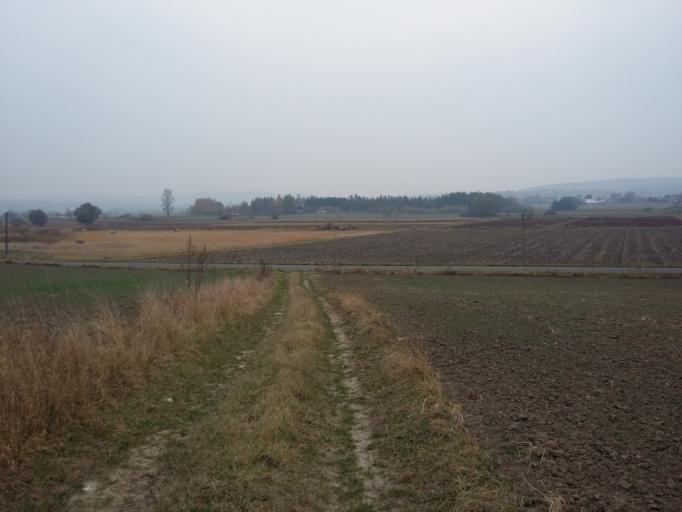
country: PL
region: Subcarpathian Voivodeship
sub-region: Powiat jasielski
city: Tarnowiec
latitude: 49.7312
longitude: 21.5653
